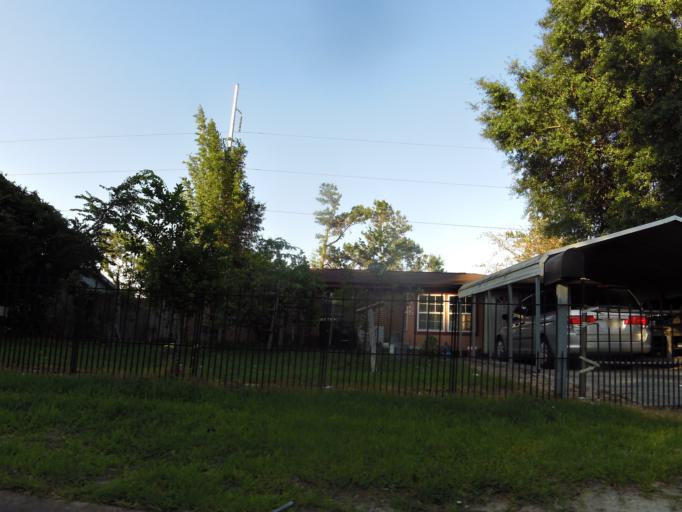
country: US
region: Florida
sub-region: Duval County
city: Jacksonville
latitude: 30.2384
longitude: -81.6024
